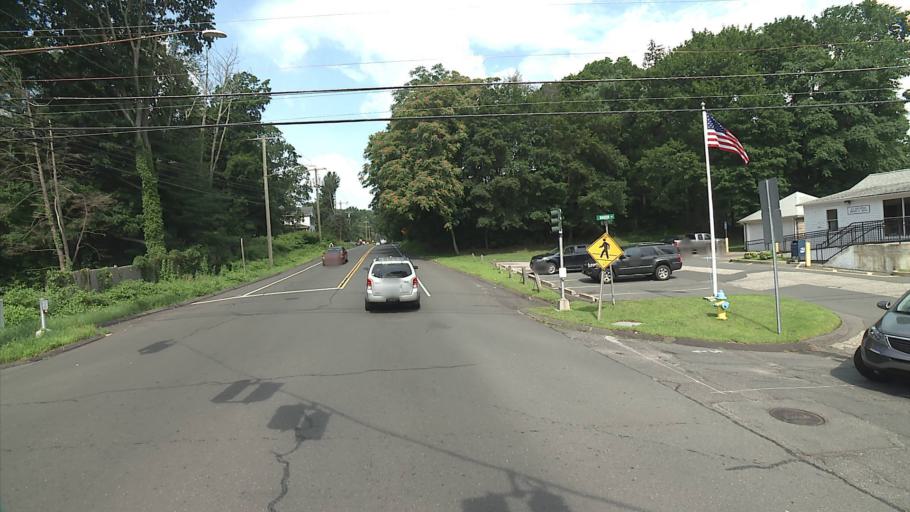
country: US
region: Connecticut
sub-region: New Haven County
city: Cheshire Village
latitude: 41.5639
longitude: -72.9257
